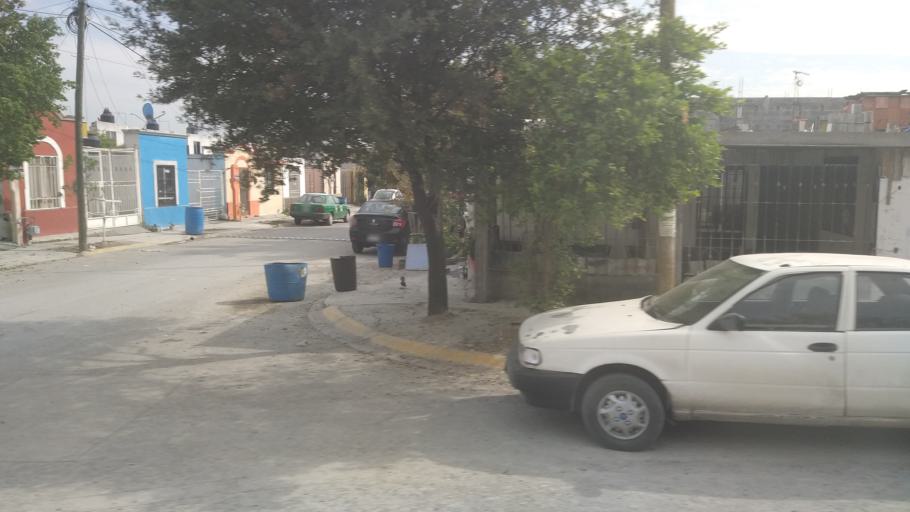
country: MX
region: Nuevo Leon
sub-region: Apodaca
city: Loma la Paz
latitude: 25.7059
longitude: -100.1422
